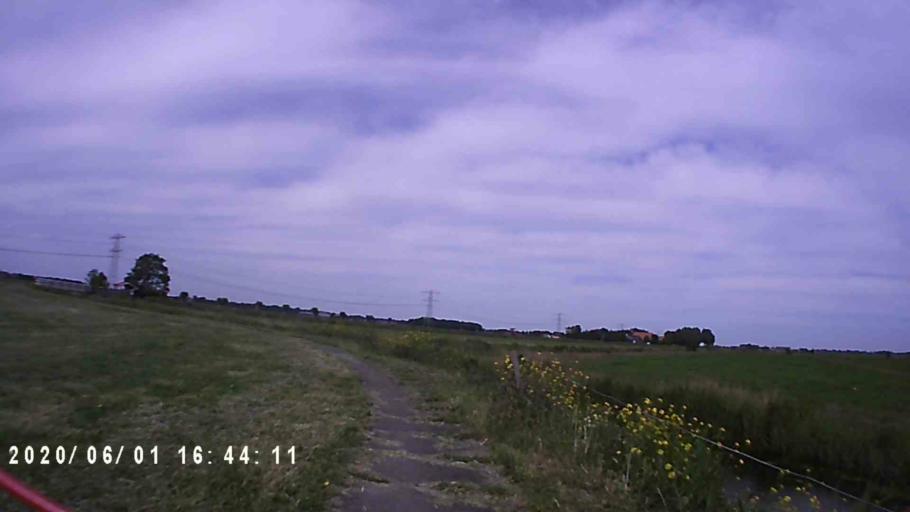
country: NL
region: Friesland
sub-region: Gemeente Boarnsterhim
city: Warten
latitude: 53.1843
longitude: 5.8828
